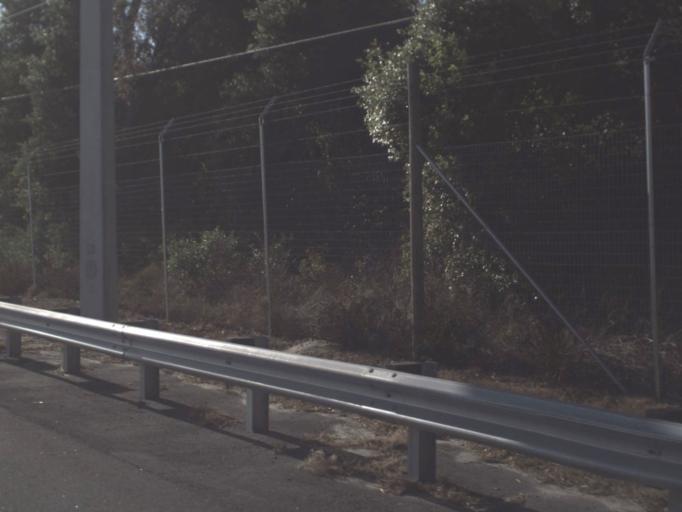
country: US
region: Florida
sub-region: Lake County
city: Mount Plymouth
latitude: 28.8128
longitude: -81.5048
